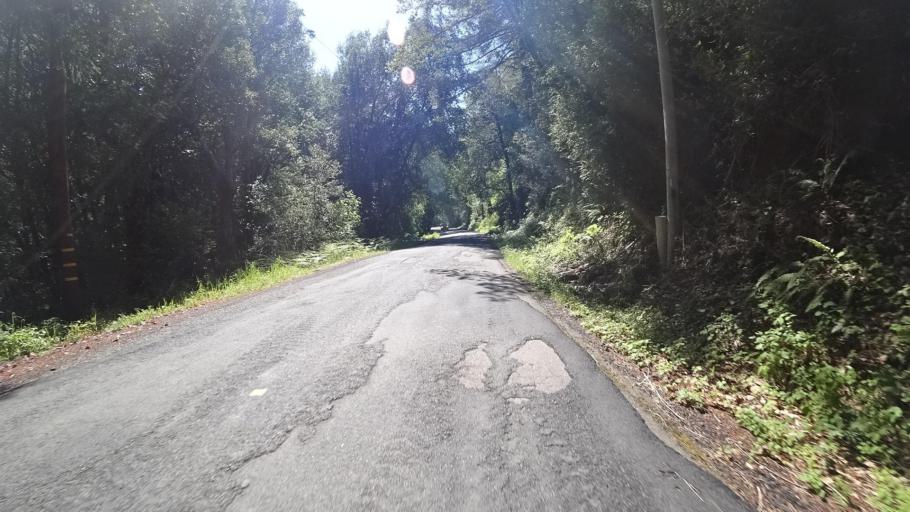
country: US
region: California
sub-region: Humboldt County
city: Rio Dell
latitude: 40.2310
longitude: -124.1524
